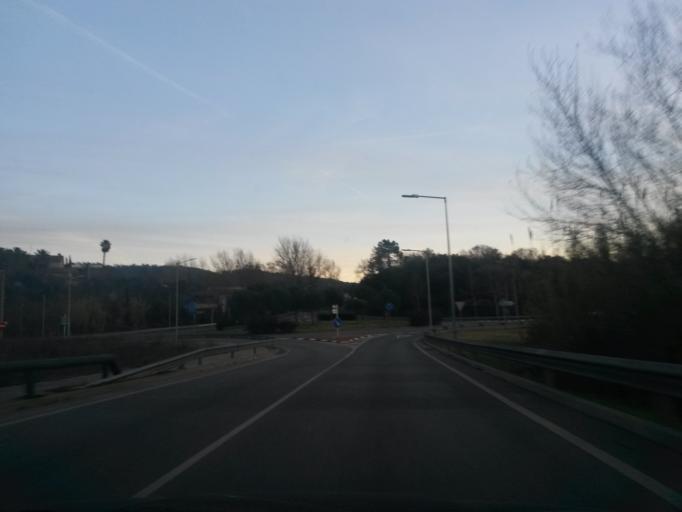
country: ES
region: Catalonia
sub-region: Provincia de Girona
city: Quart d'Onyar
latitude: 41.9647
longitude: 2.8432
